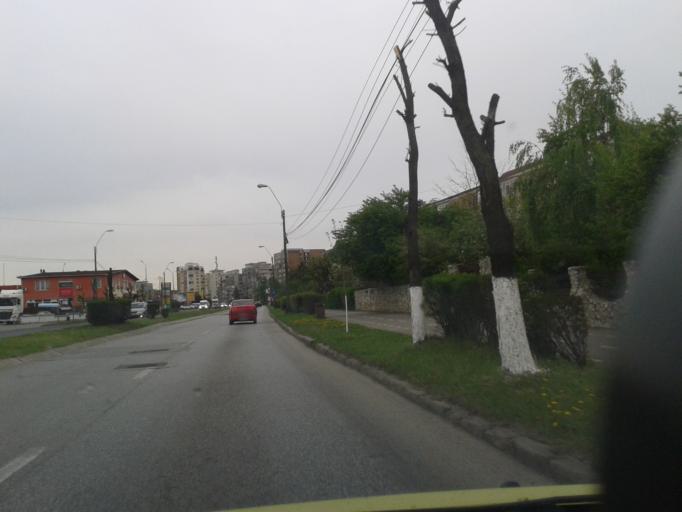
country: RO
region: Hunedoara
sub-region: Municipiul Deva
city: Deva
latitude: 45.8871
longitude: 22.9074
